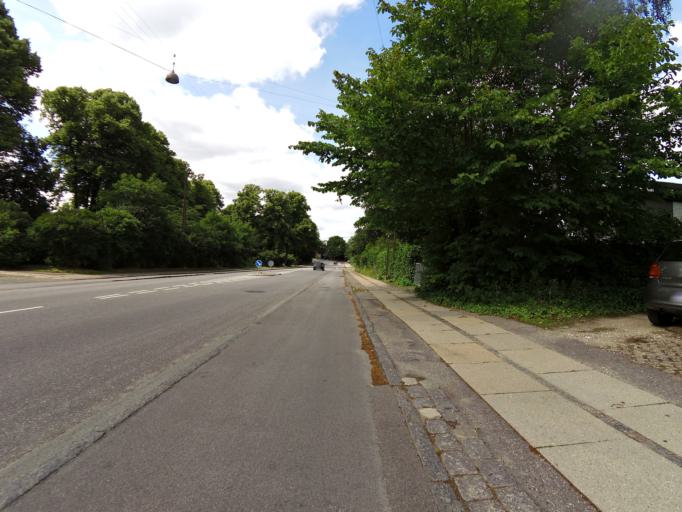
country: DK
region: Capital Region
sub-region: Frederiksberg Kommune
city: Frederiksberg
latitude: 55.7209
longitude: 12.5478
